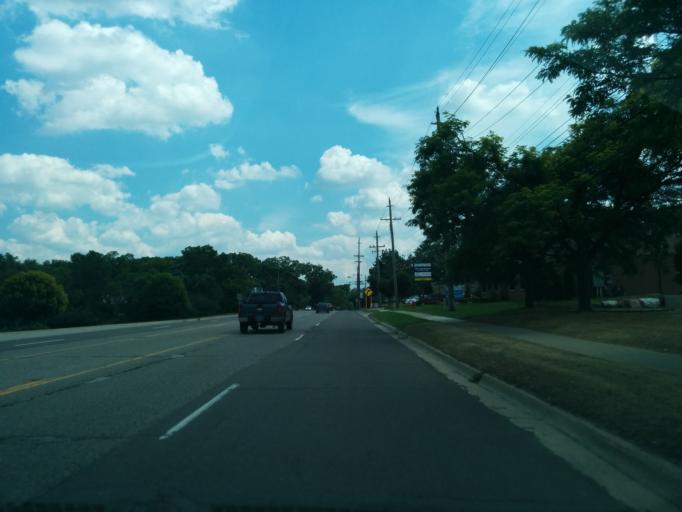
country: US
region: Michigan
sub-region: Oakland County
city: Farmington
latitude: 42.4687
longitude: -83.3885
